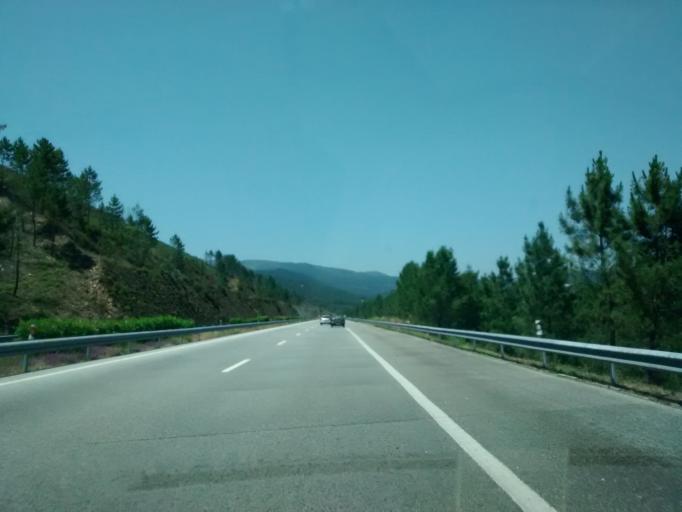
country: PT
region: Viana do Castelo
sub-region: Paredes de Coura
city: Paredes de Coura
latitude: 41.8764
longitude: -8.6594
